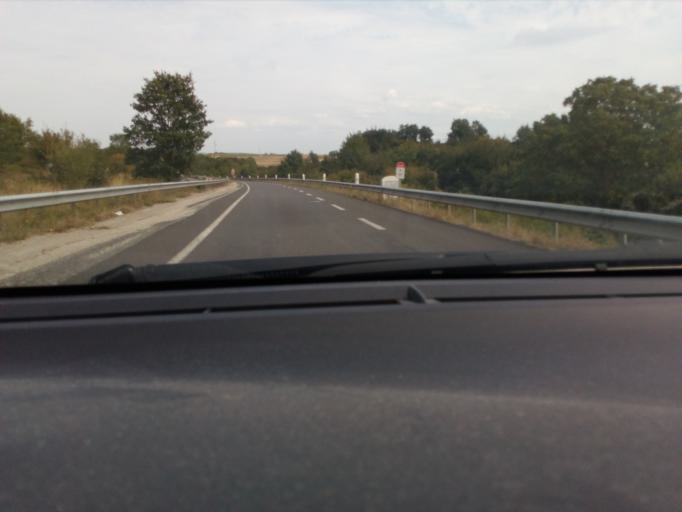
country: FR
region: Poitou-Charentes
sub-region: Departement de la Charente
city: Saint-Saturnin
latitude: 45.6703
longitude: 0.0338
